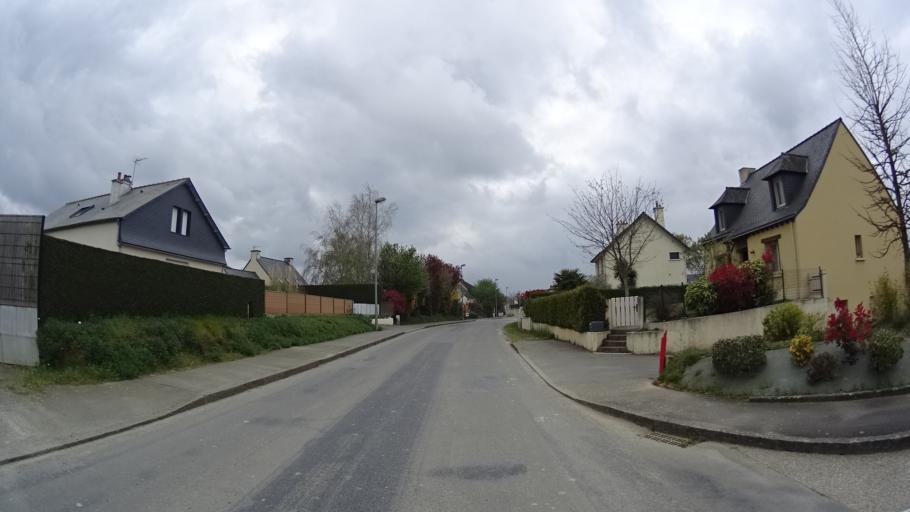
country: FR
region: Brittany
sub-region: Departement d'Ille-et-Vilaine
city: Cintre
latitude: 48.1066
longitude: -1.8662
